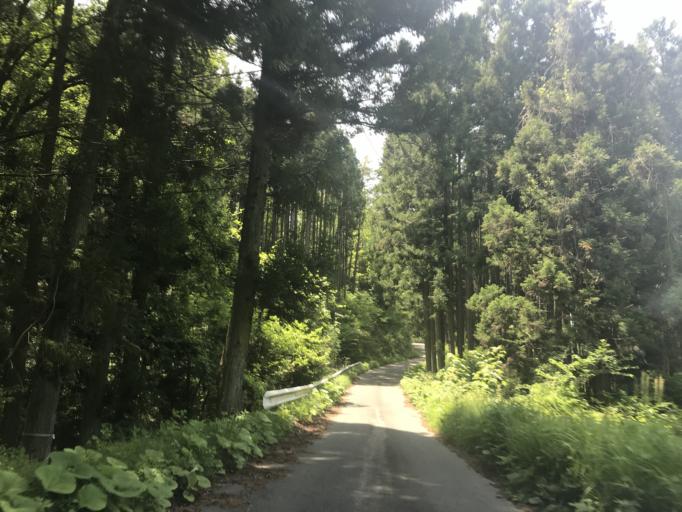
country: JP
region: Iwate
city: Ichinoseki
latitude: 38.9697
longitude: 141.2240
